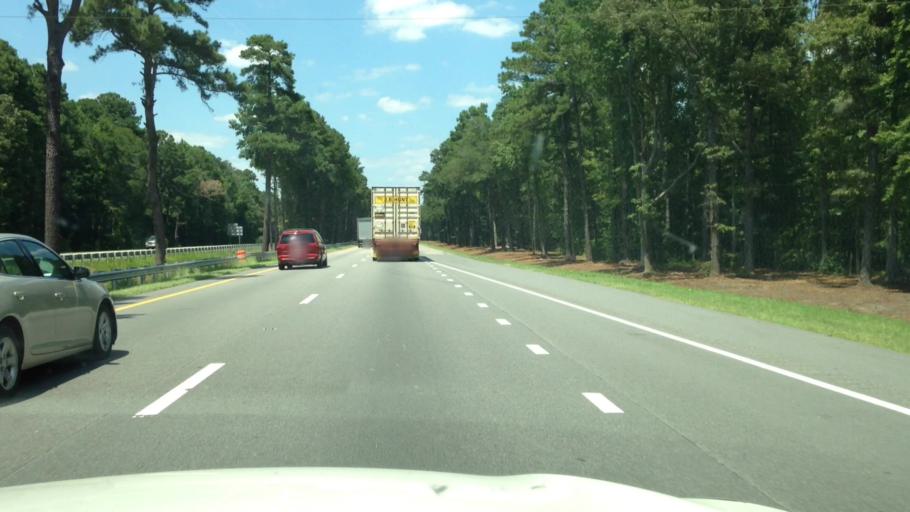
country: US
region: North Carolina
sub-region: Robeson County
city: Lumberton
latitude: 34.6787
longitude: -79.0030
